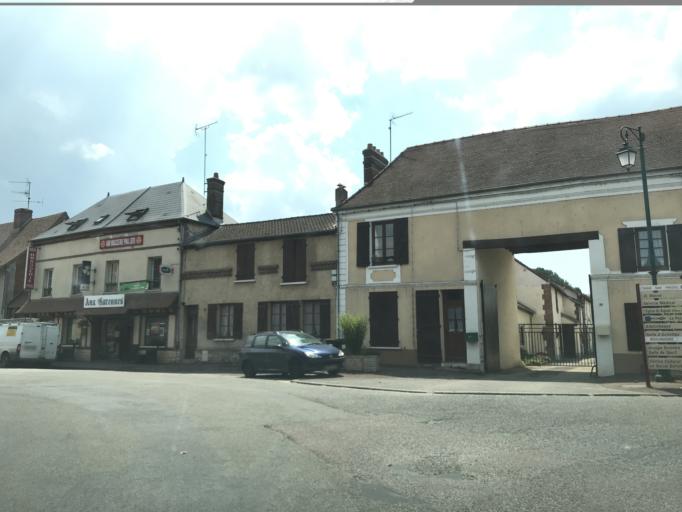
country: FR
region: Haute-Normandie
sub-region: Departement de l'Eure
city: Garennes-sur-Eure
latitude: 48.9096
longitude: 1.4410
